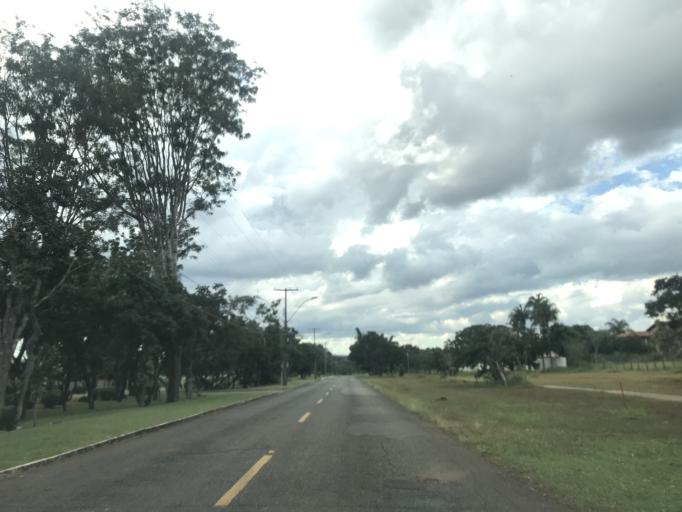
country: BR
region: Federal District
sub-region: Brasilia
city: Brasilia
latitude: -15.9021
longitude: -47.9392
